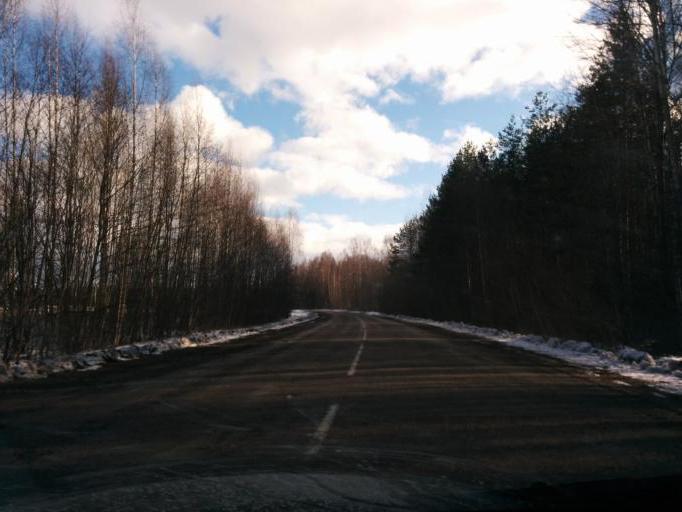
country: LV
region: Balvu Rajons
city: Balvi
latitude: 57.1655
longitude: 27.1400
